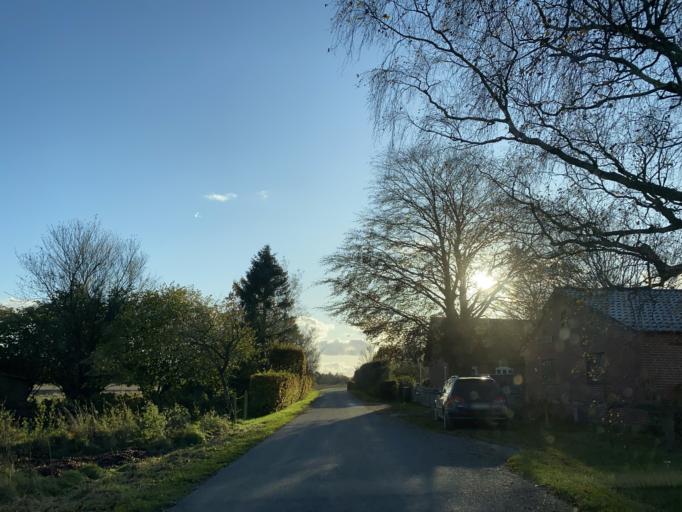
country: DK
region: Central Jutland
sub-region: Viborg Kommune
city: Bjerringbro
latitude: 56.3184
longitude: 9.6992
